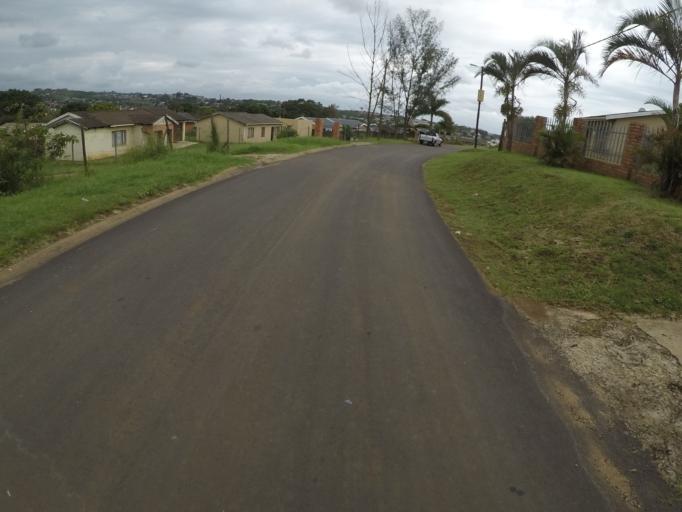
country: ZA
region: KwaZulu-Natal
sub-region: uThungulu District Municipality
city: Empangeni
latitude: -28.7839
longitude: 31.8552
